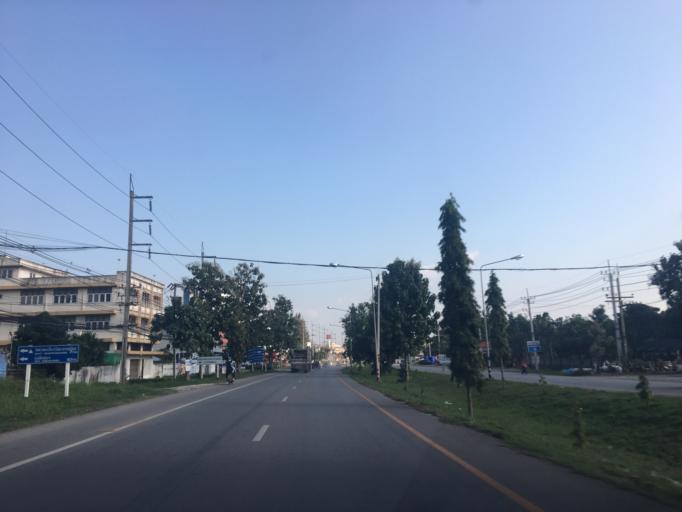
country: TH
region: Phayao
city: Phayao
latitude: 19.1799
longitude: 99.8993
